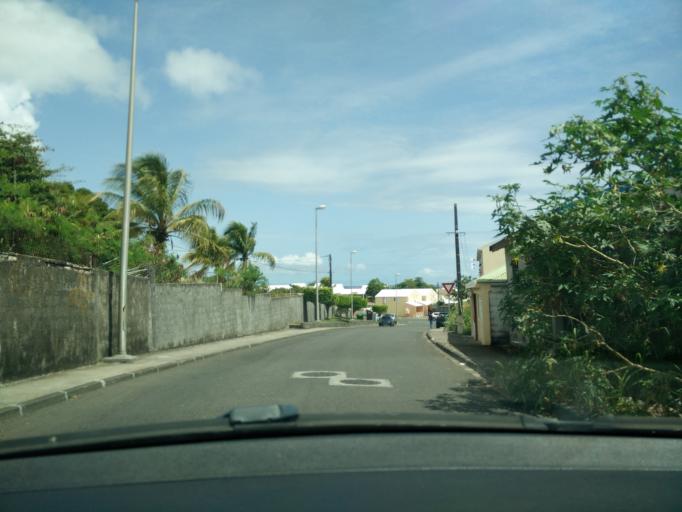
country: GP
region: Guadeloupe
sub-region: Guadeloupe
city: Le Moule
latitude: 16.3284
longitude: -61.3468
